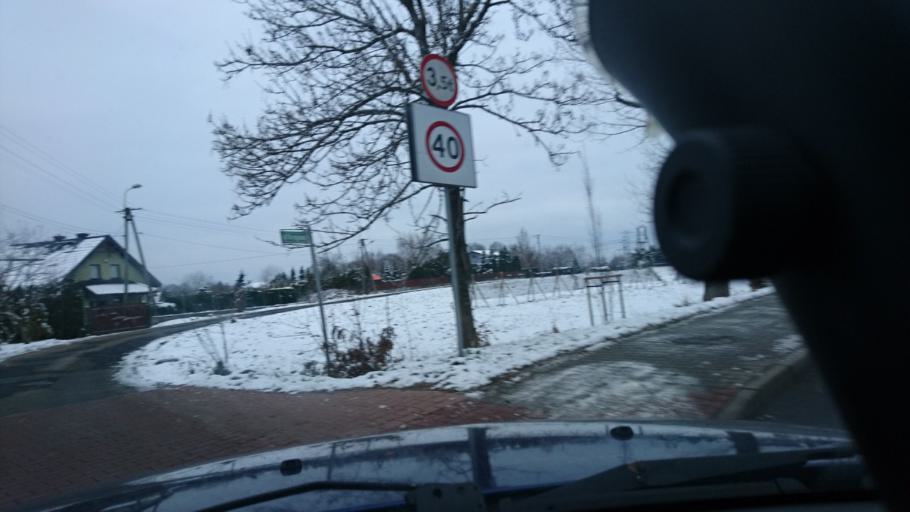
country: PL
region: Silesian Voivodeship
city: Janowice
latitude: 49.8591
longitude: 19.1128
